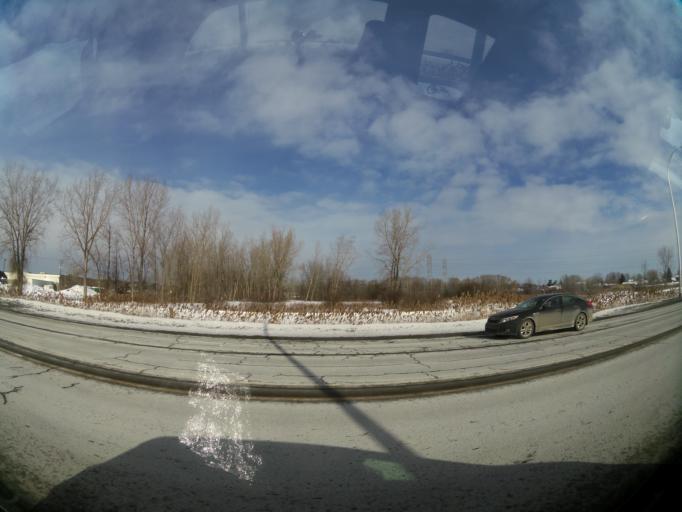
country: CA
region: Quebec
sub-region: Outaouais
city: Gatineau
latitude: 45.4833
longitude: -75.6598
